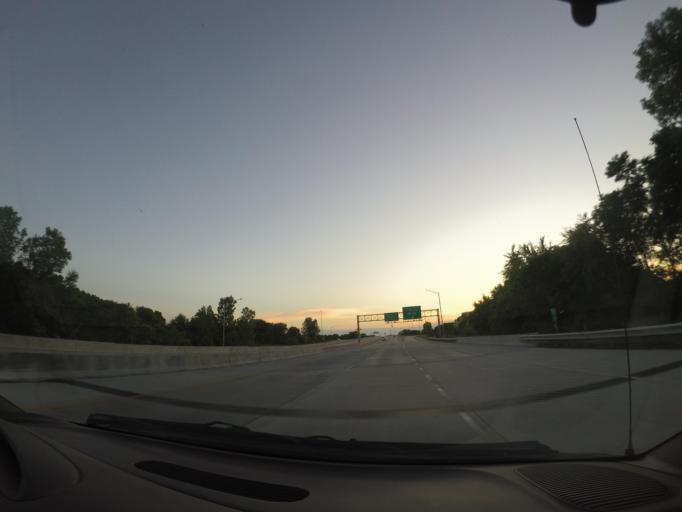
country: US
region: Indiana
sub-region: Elkhart County
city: Dunlap
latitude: 41.6671
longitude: -85.8799
